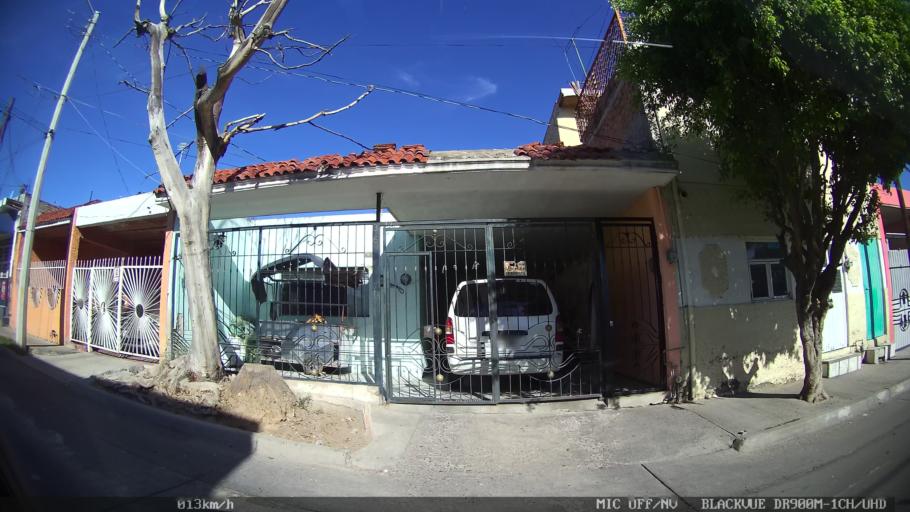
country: MX
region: Jalisco
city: Tlaquepaque
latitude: 20.6983
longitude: -103.2774
